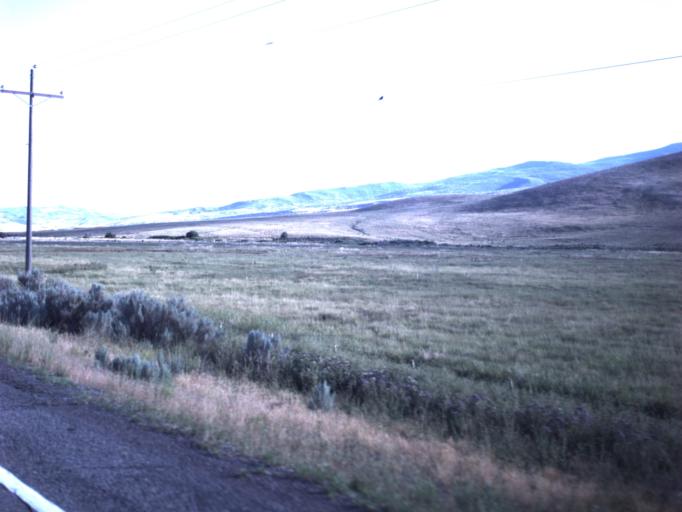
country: US
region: Utah
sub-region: Sanpete County
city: Fairview
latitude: 39.8228
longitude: -111.5091
